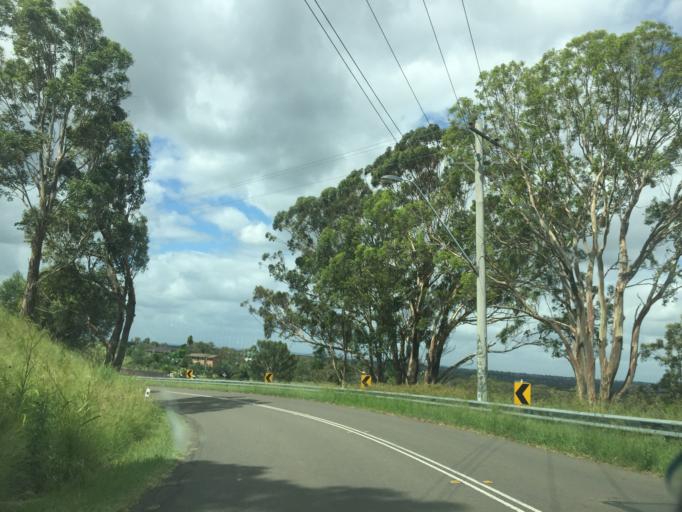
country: AU
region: New South Wales
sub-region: Penrith Municipality
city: Kingswood Park
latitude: -33.7929
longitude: 150.7371
